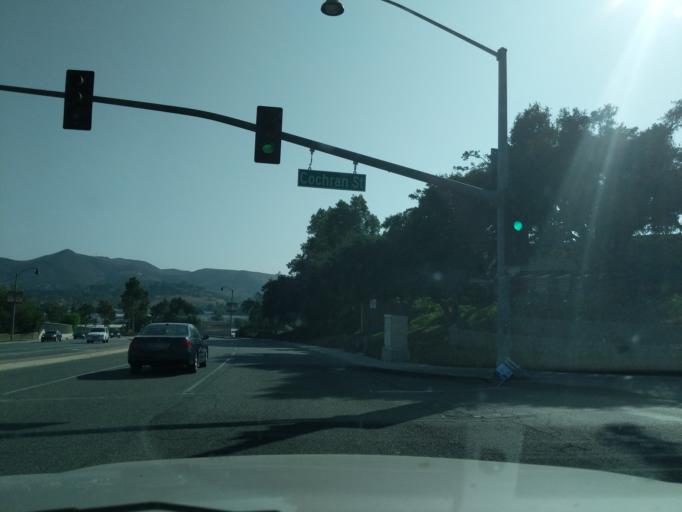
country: US
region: California
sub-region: Ventura County
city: Simi Valley
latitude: 34.2818
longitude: -118.7953
